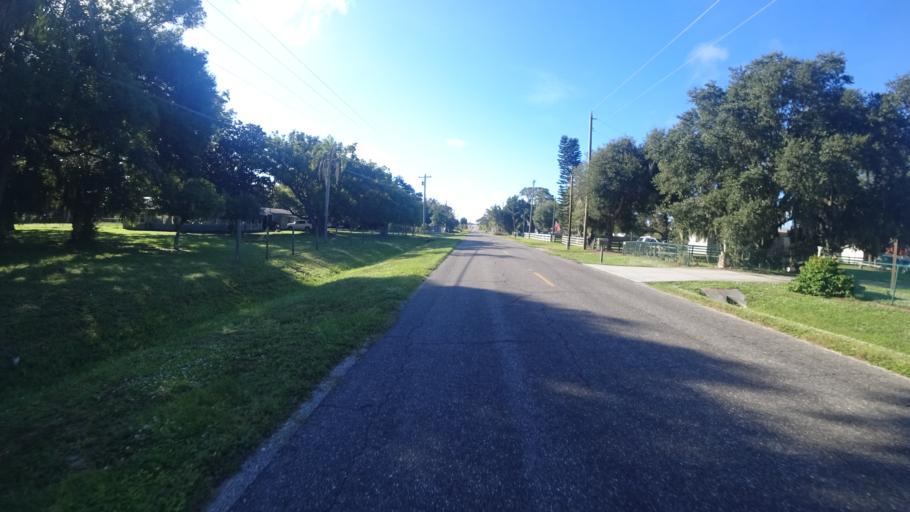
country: US
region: Florida
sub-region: Manatee County
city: Memphis
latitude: 27.5938
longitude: -82.5273
